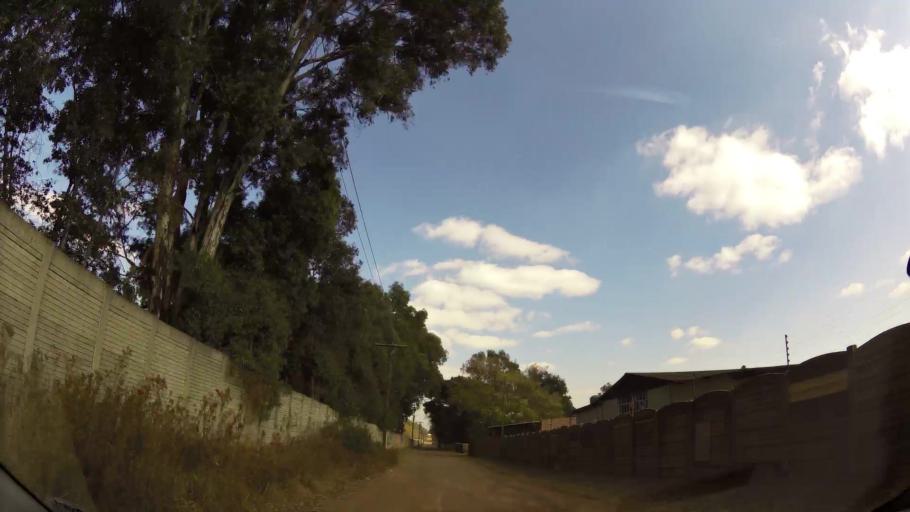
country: ZA
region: Gauteng
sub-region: Ekurhuleni Metropolitan Municipality
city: Benoni
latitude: -26.1059
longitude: 28.3658
